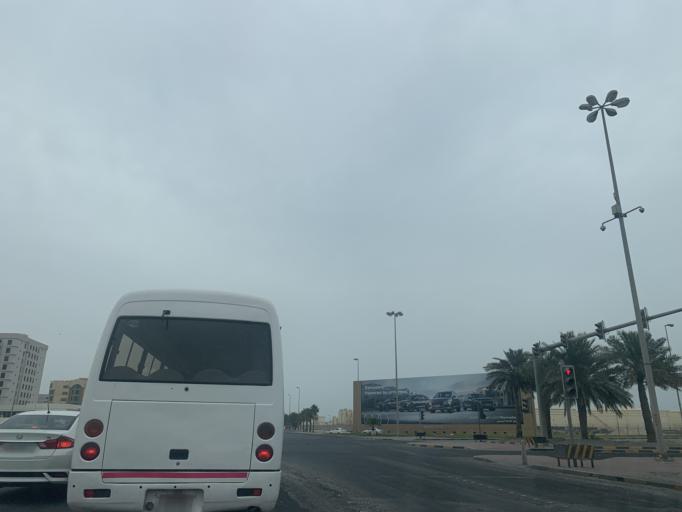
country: BH
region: Muharraq
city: Al Hadd
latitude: 26.2248
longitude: 50.6578
